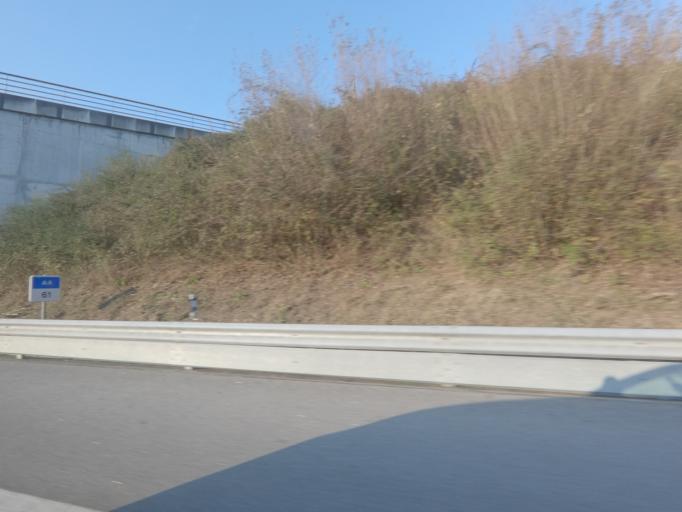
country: PT
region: Porto
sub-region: Amarante
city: Amarante
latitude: 41.2588
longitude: -8.0552
